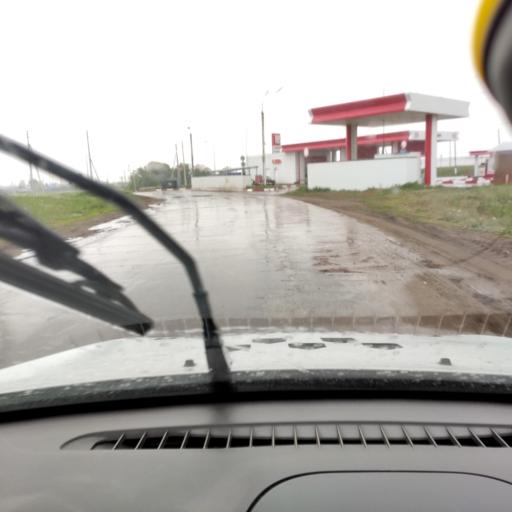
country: RU
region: Samara
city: Zhigulevsk
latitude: 53.5563
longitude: 49.5363
